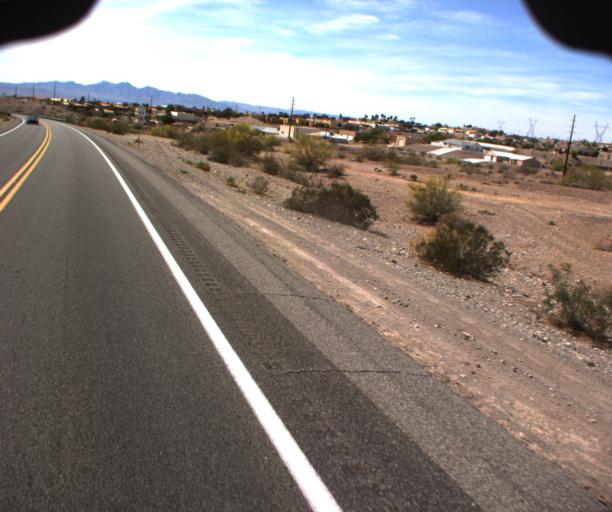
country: US
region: Arizona
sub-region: Mohave County
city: Lake Havasu City
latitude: 34.4504
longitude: -114.2463
